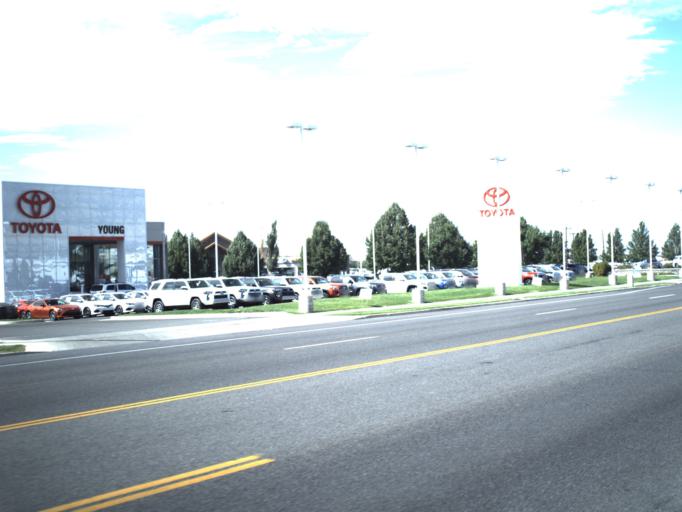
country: US
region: Utah
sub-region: Cache County
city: North Logan
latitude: 41.7669
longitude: -111.8341
